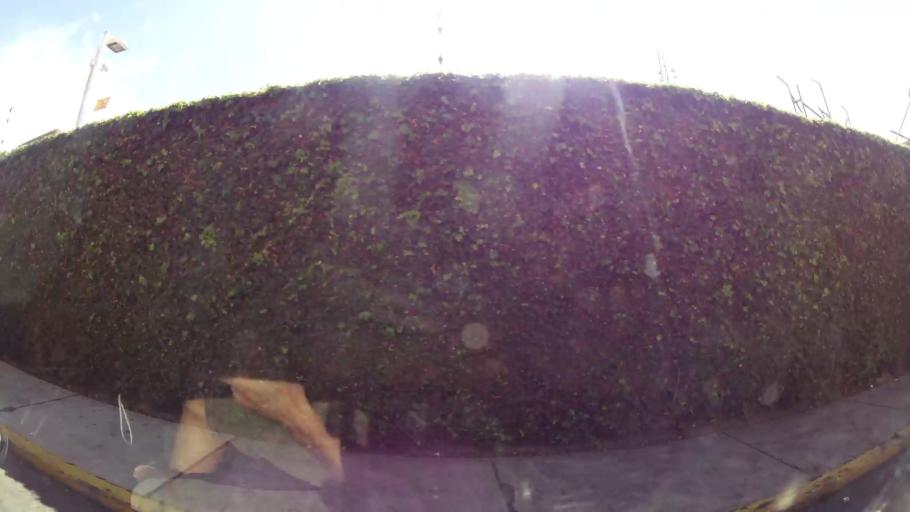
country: EC
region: Pichincha
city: Quito
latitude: -0.1998
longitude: -78.4326
